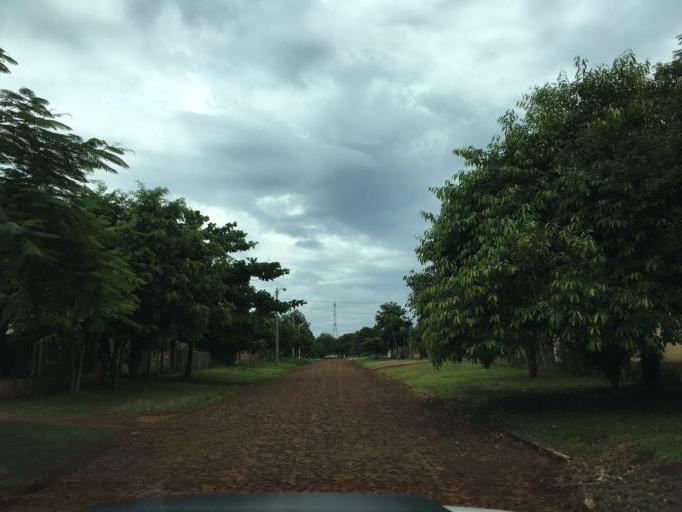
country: PY
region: Alto Parana
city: Ciudad del Este
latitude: -25.4145
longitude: -54.6547
